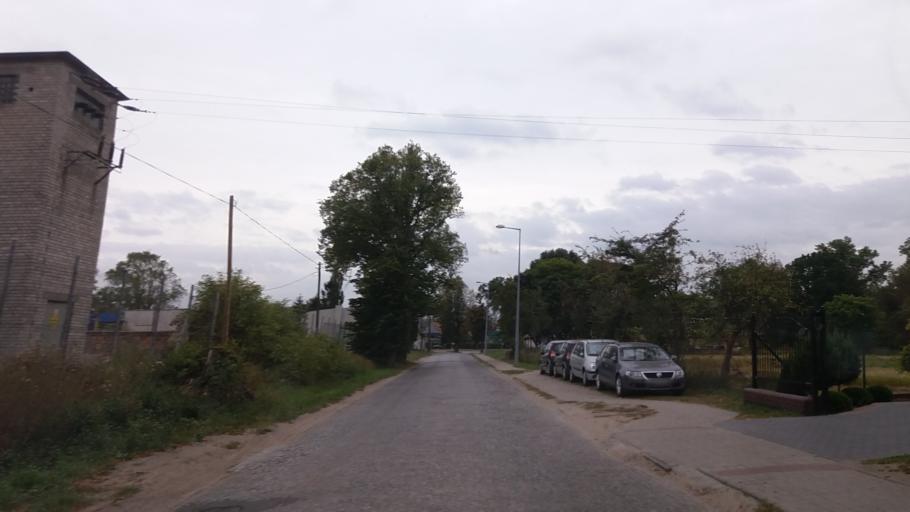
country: PL
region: Lubusz
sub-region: Powiat strzelecko-drezdenecki
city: Strzelce Krajenskie
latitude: 52.8828
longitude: 15.5409
